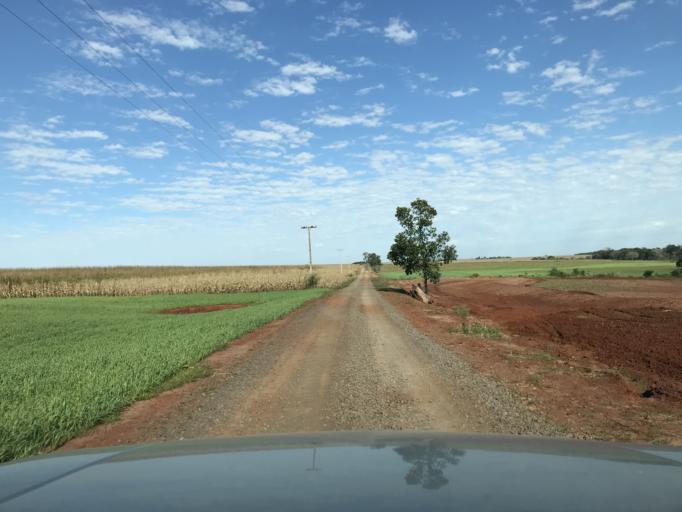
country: BR
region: Parana
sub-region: Palotina
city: Palotina
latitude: -24.1636
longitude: -53.7494
